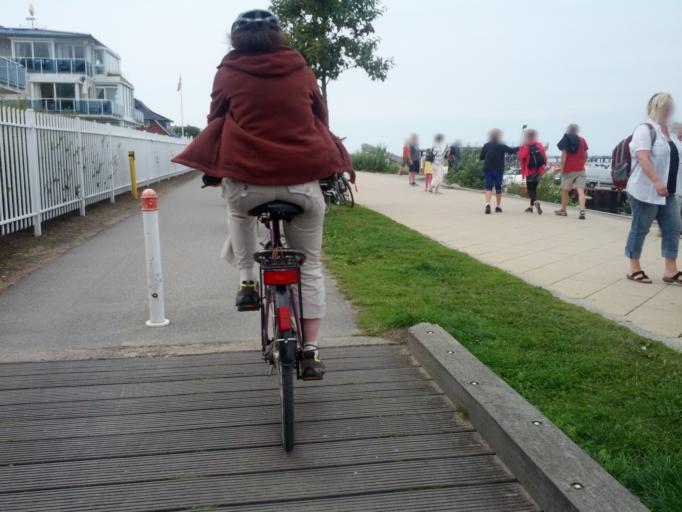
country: DE
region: Mecklenburg-Vorpommern
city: Ostseebad Kuhlungsborn
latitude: 54.1521
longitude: 11.7679
